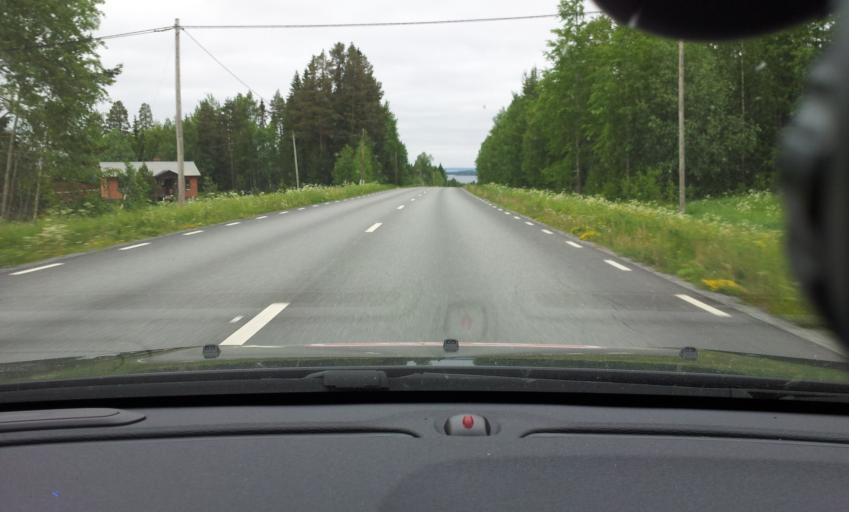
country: SE
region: Jaemtland
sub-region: Krokoms Kommun
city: Krokom
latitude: 63.1147
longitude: 14.2931
